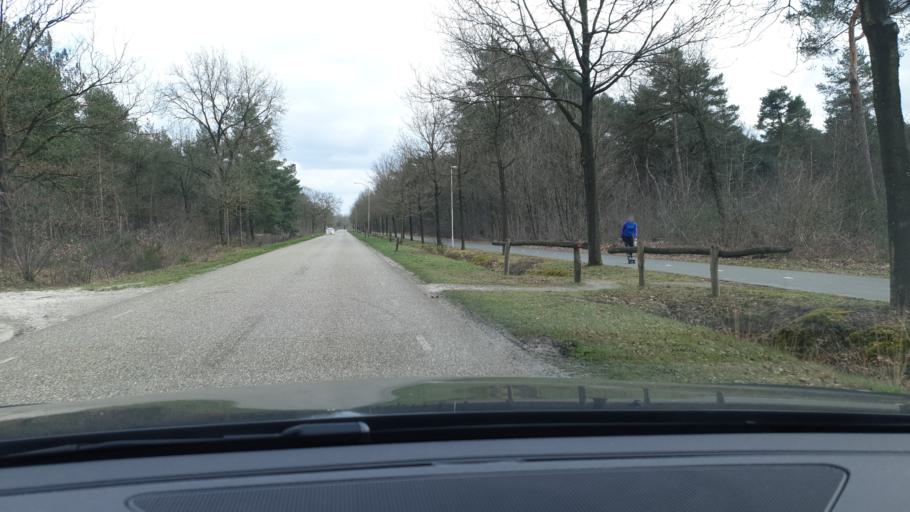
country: NL
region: North Brabant
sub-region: Gemeente Oirschot
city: Oostelbeers
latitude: 51.4593
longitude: 5.2763
